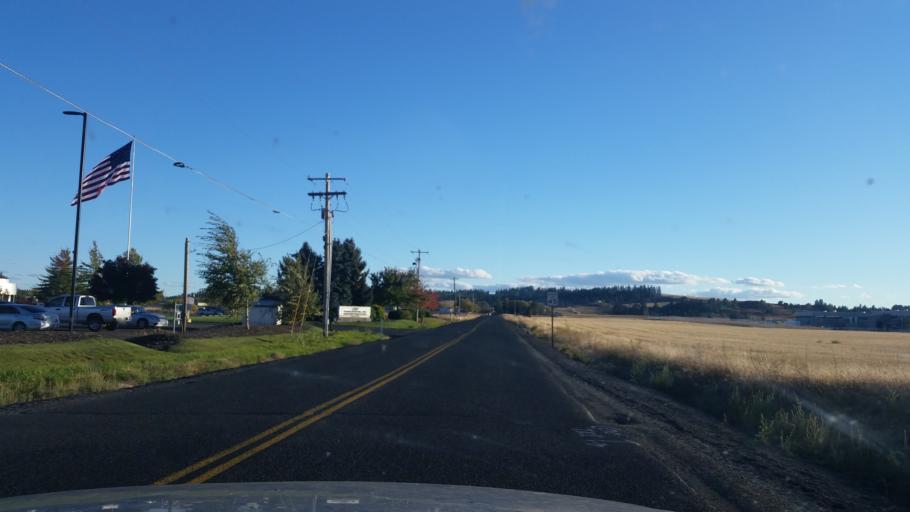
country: US
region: Washington
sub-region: Spokane County
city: Airway Heights
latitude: 47.5872
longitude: -117.5646
